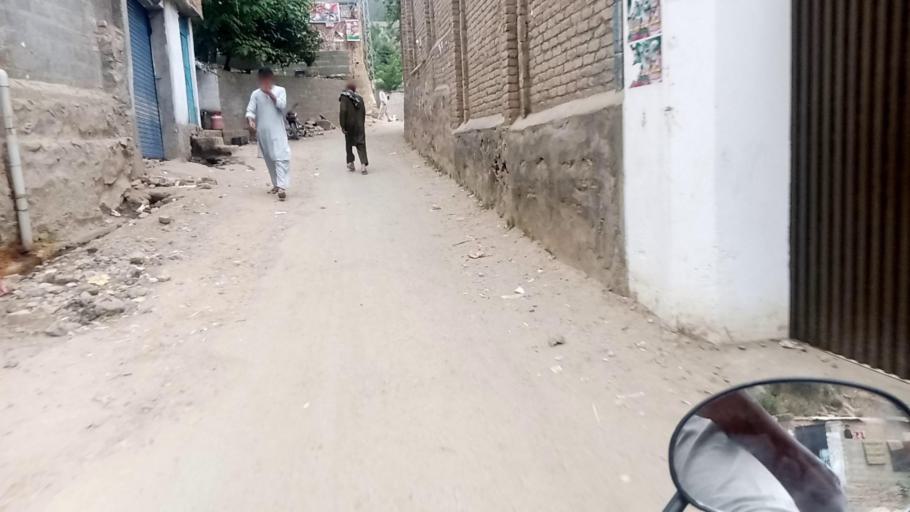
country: PK
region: Khyber Pakhtunkhwa
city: Saidu Sharif
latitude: 34.7272
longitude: 72.3646
